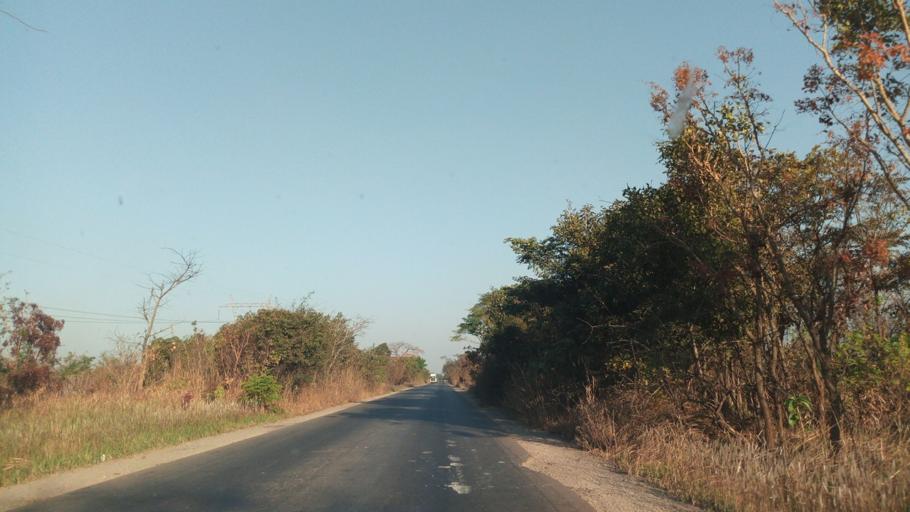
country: CD
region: Katanga
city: Likasi
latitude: -11.1182
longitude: 27.0296
